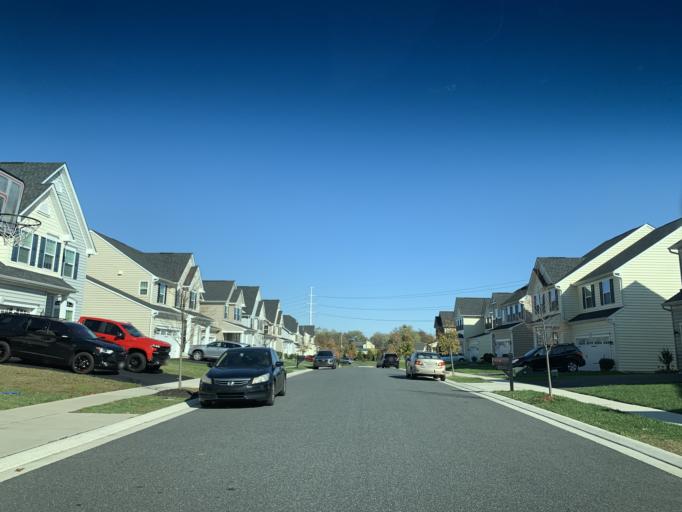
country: US
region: Maryland
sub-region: Baltimore County
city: White Marsh
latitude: 39.4028
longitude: -76.4107
